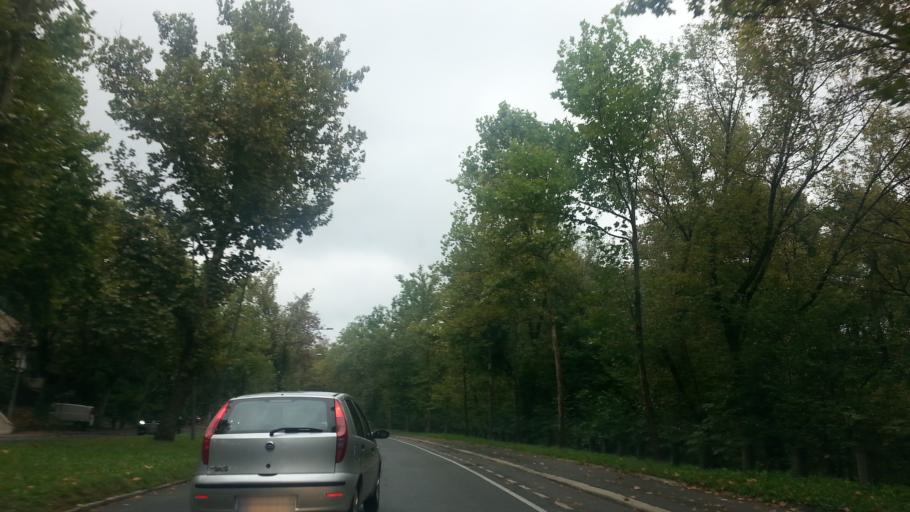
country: RS
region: Central Serbia
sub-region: Belgrade
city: Vozdovac
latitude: 44.7790
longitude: 20.4691
